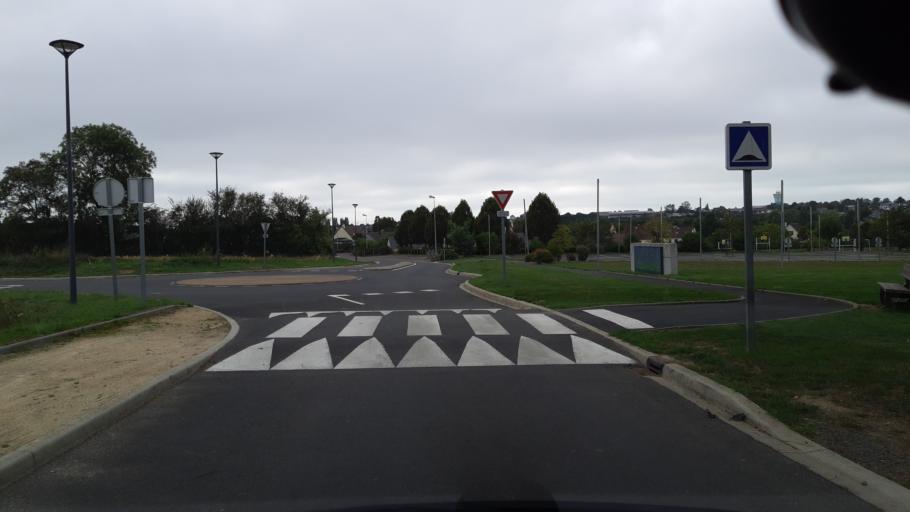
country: FR
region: Lower Normandy
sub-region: Departement de la Manche
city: Donville-les-Bains
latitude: 48.8437
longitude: -1.5531
